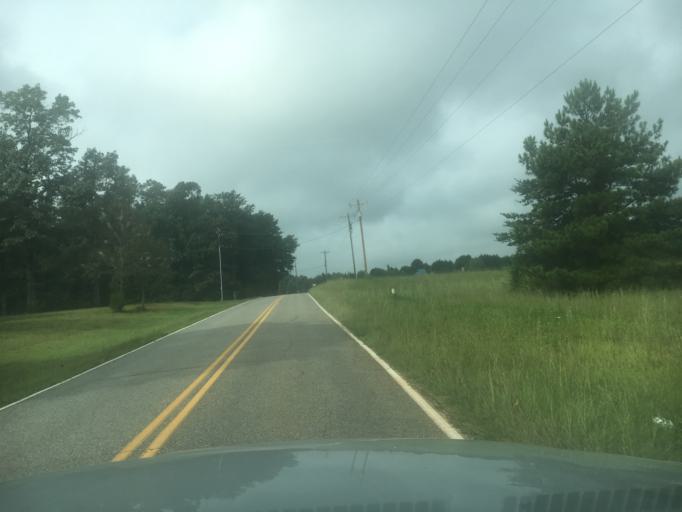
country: US
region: South Carolina
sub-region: Spartanburg County
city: Landrum
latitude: 35.1698
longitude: -82.0662
